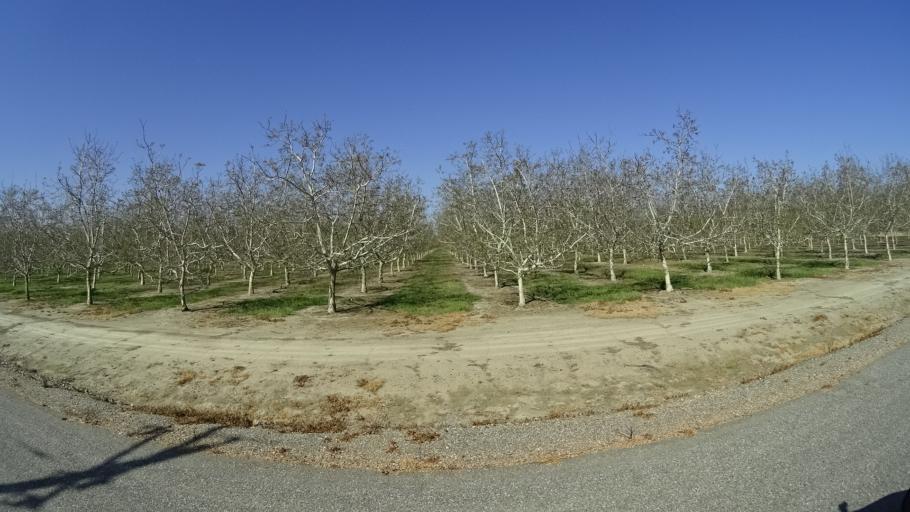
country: US
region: California
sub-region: Glenn County
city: Hamilton City
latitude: 39.6333
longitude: -122.0274
